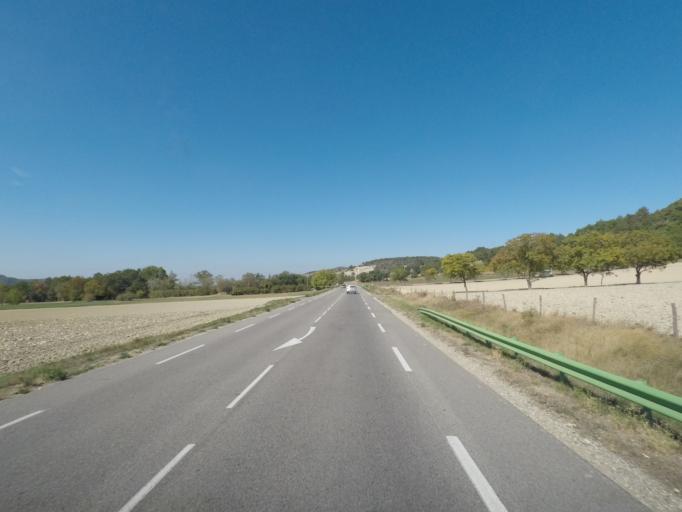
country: FR
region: Rhone-Alpes
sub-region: Departement de la Drome
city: Aouste-sur-Sye
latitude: 44.7000
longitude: 5.1246
